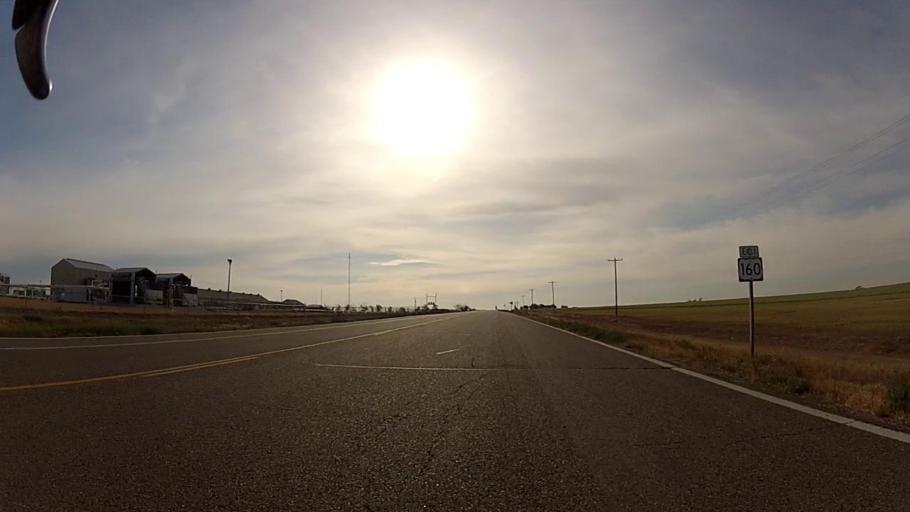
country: US
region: Kansas
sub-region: Grant County
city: Ulysses
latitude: 37.5766
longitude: -101.4897
